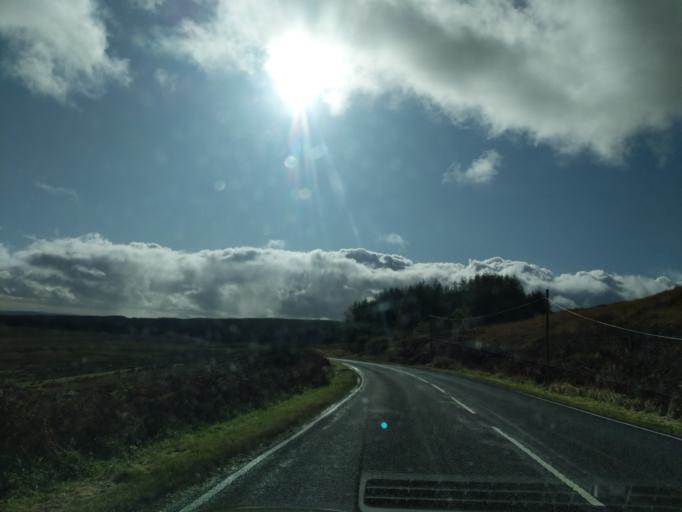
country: GB
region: Scotland
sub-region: Dumfries and Galloway
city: Moffat
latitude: 55.3919
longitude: -3.4832
